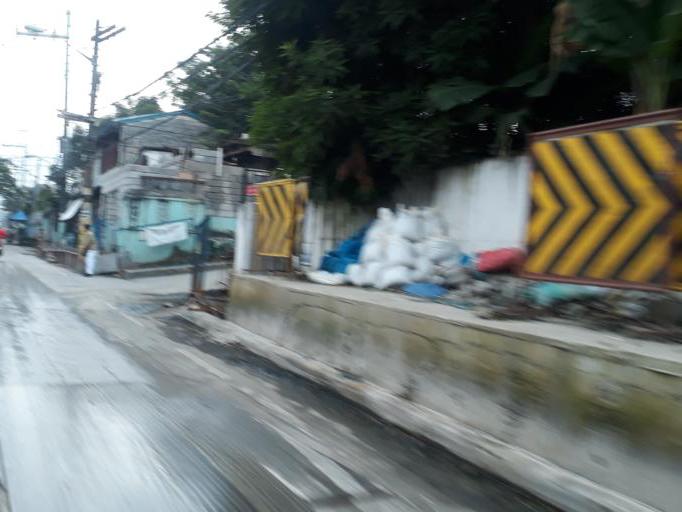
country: PH
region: Central Luzon
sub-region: Province of Bulacan
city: Obando
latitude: 14.7044
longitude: 120.9484
